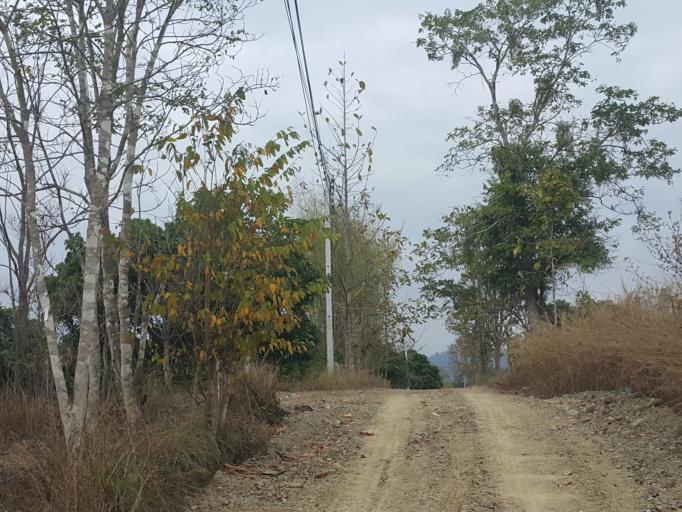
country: TH
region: Chiang Mai
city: Hang Dong
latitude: 18.7073
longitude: 98.8729
